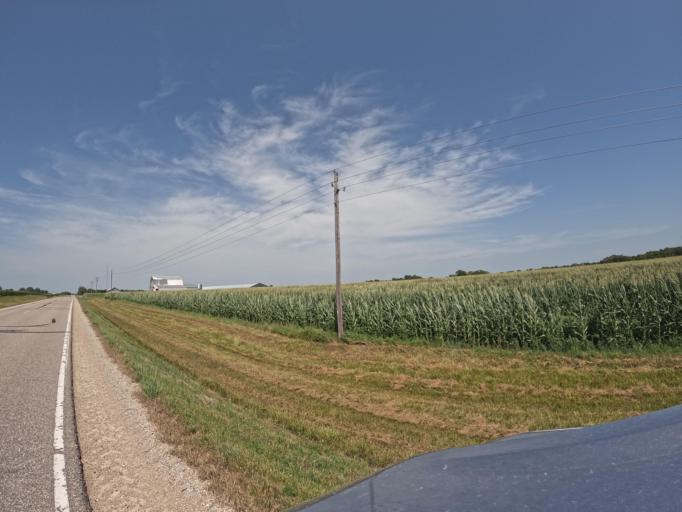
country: US
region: Iowa
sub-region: Henry County
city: Mount Pleasant
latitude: 40.9970
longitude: -91.6121
